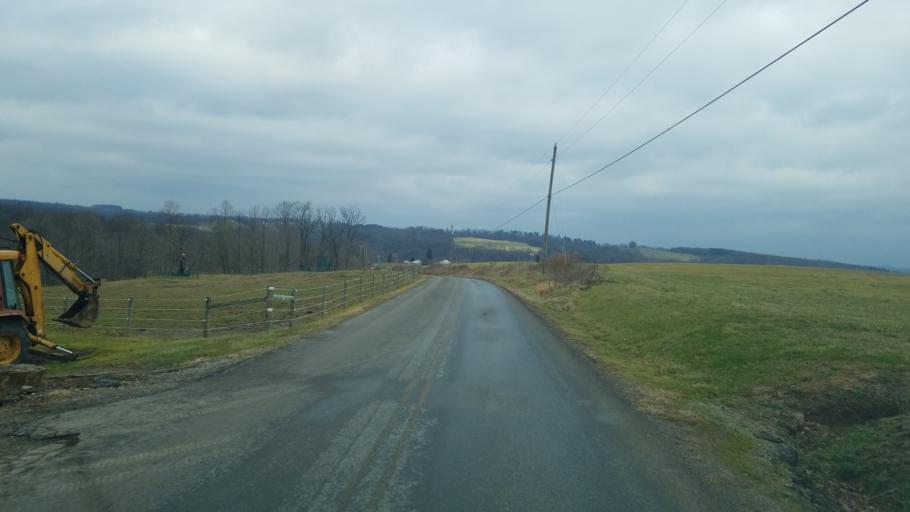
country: US
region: Ohio
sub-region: Holmes County
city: Millersburg
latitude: 40.5894
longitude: -81.9678
